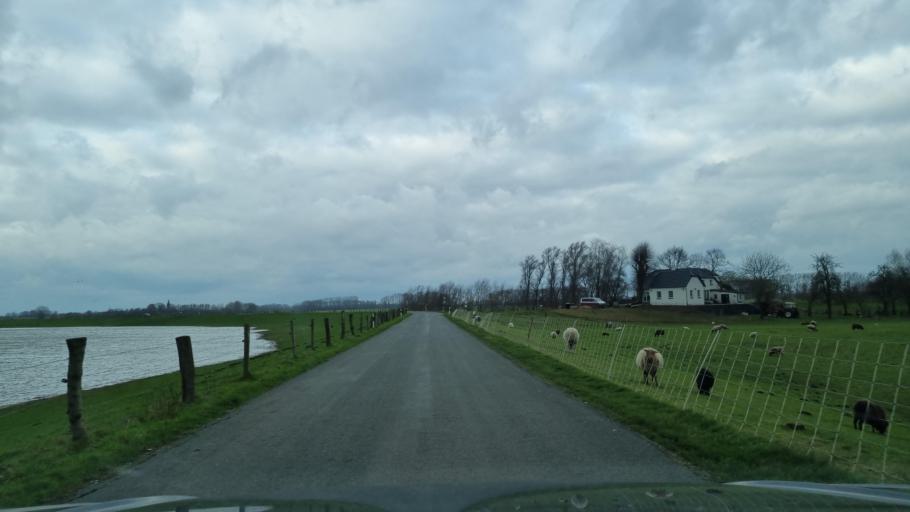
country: DE
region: North Rhine-Westphalia
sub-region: Regierungsbezirk Dusseldorf
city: Kleve
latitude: 51.8324
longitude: 6.1322
